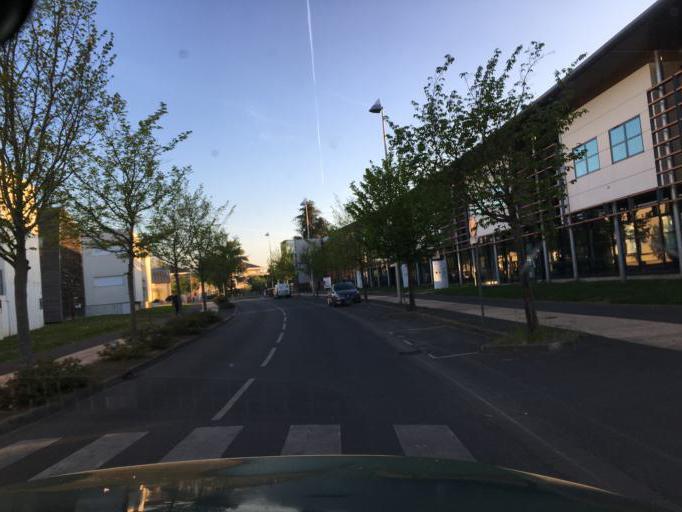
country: FR
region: Centre
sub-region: Departement du Loiret
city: Orleans
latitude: 47.8881
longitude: 1.8988
